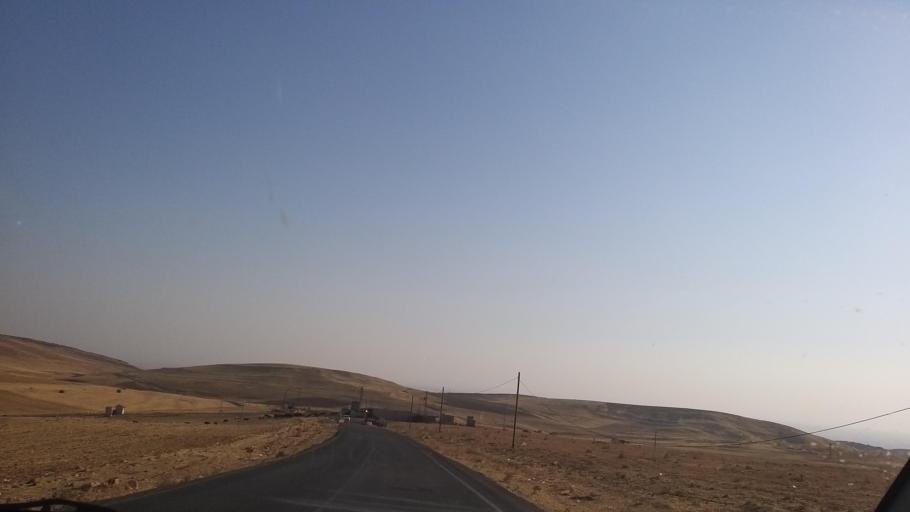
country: TR
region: Diyarbakir
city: Silvan
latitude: 38.1873
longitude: 41.0074
